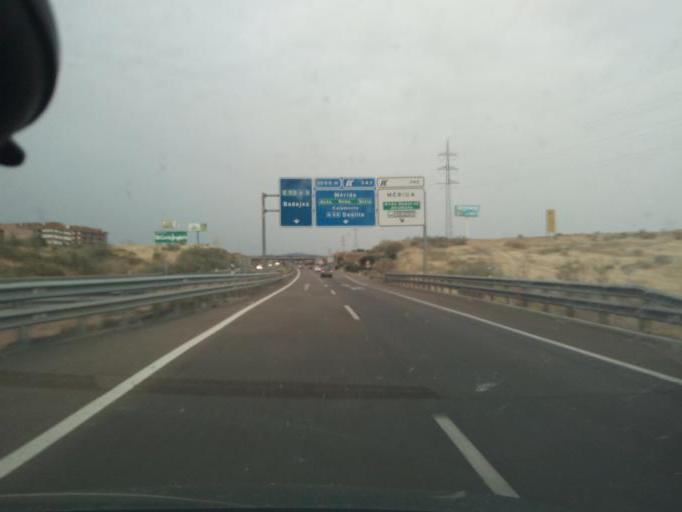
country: ES
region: Extremadura
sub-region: Provincia de Badajoz
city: Merida
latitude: 38.9260
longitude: -6.3699
